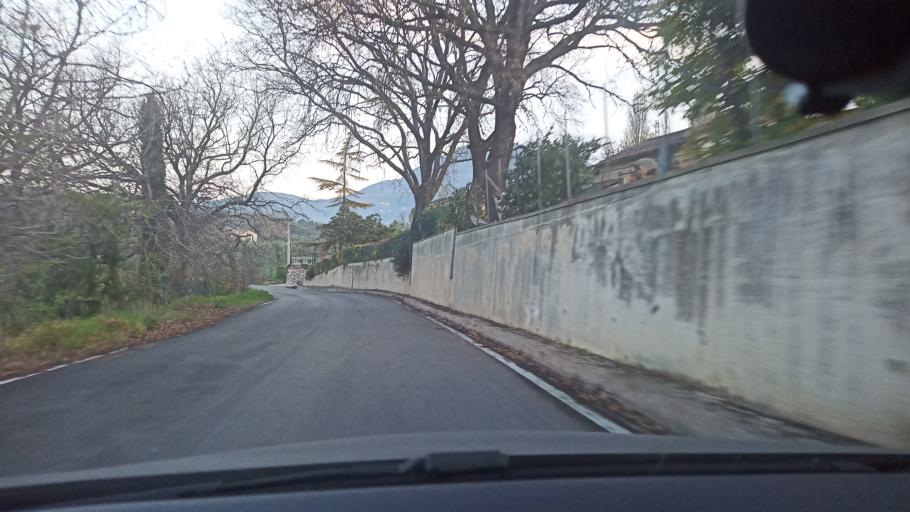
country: IT
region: Latium
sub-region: Provincia di Rieti
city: Vacone
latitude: 42.3646
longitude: 12.6606
